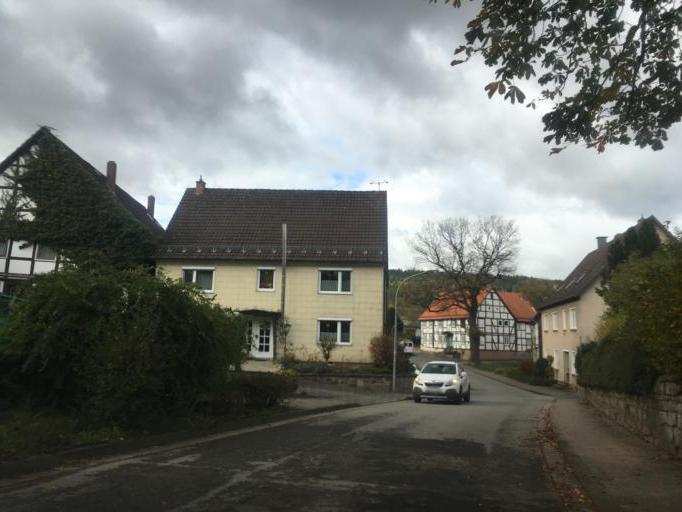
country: DE
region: Lower Saxony
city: Bodenfelde
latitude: 51.6400
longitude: 9.5521
